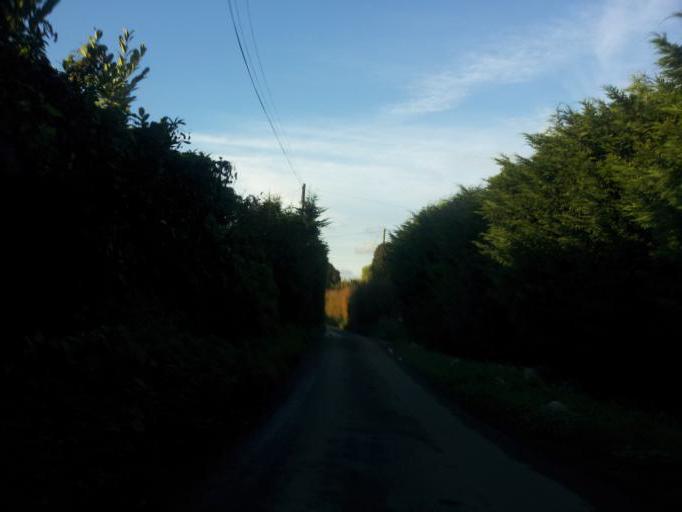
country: GB
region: England
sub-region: Kent
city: Newington
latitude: 51.3668
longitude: 0.6546
